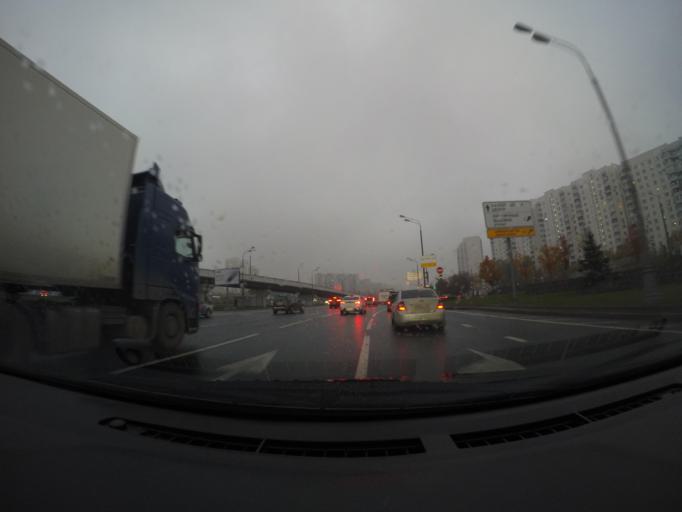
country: RU
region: Moscow
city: Annino
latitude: 55.5788
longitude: 37.5964
